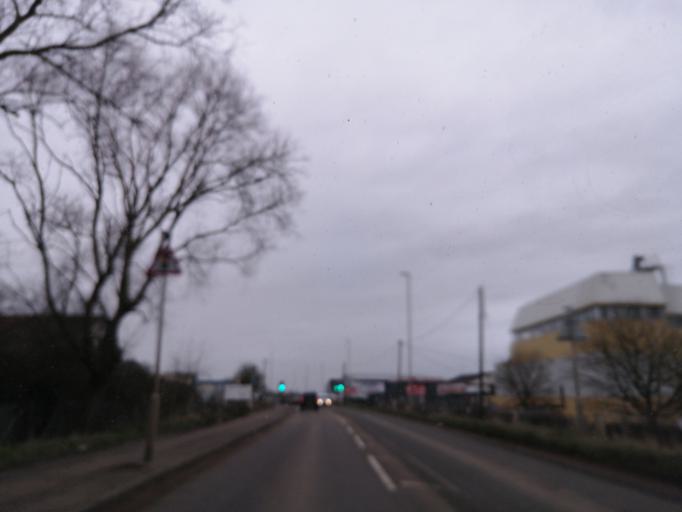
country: GB
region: England
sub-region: Cambridgeshire
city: Yaxley
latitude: 52.5250
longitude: -0.2409
